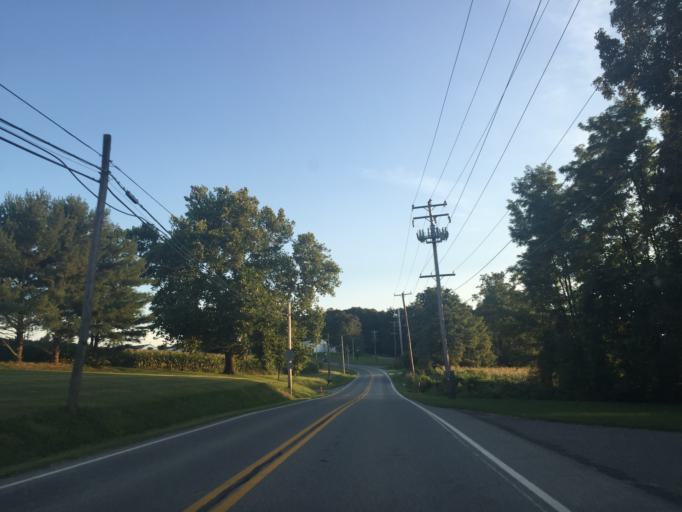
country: US
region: Pennsylvania
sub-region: York County
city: Susquehanna Trails
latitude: 39.7391
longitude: -76.3253
